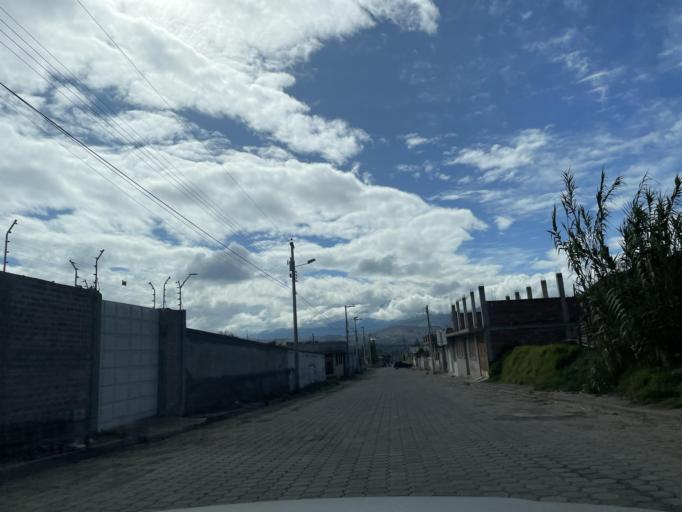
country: EC
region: Chimborazo
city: Guano
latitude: -1.6087
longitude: -78.6299
